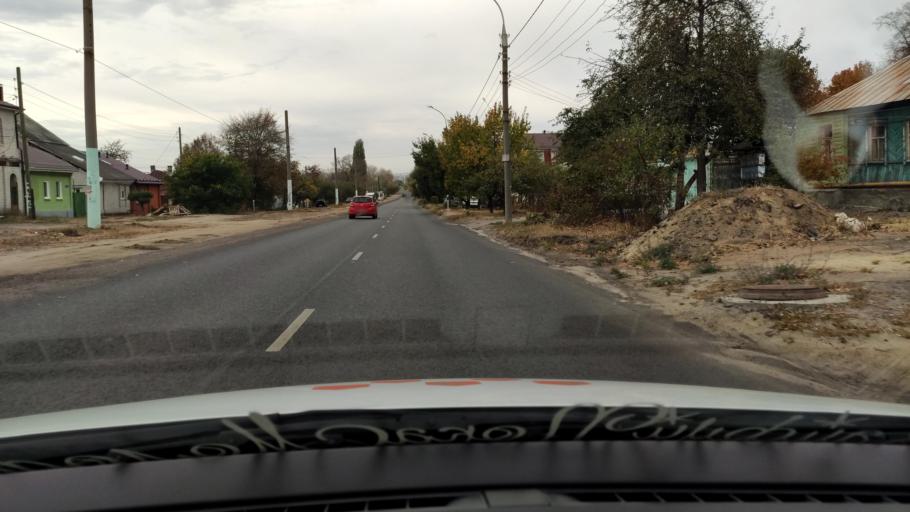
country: RU
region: Voronezj
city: Voronezh
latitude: 51.6978
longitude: 39.1740
